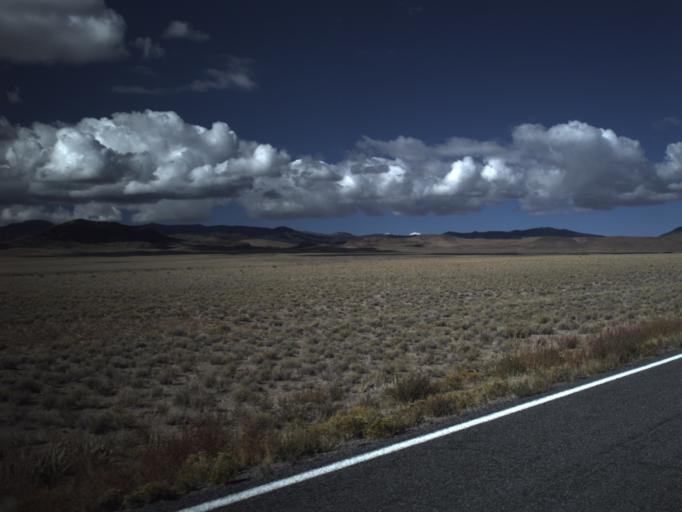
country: US
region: Utah
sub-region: Beaver County
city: Milford
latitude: 38.5705
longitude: -113.7852
